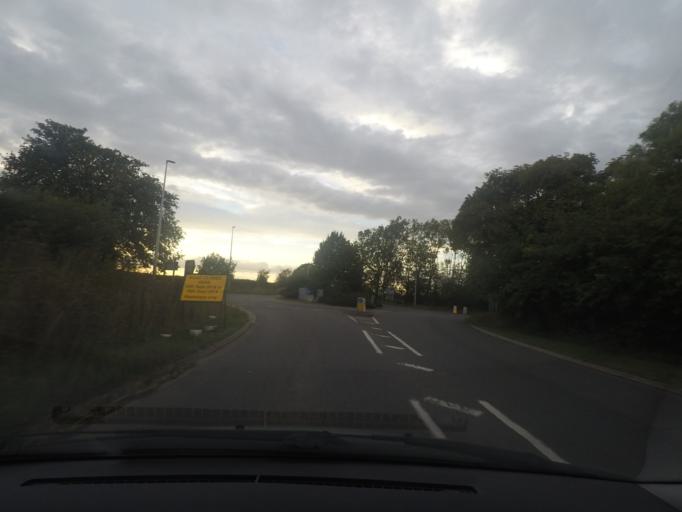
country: GB
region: England
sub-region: North East Lincolnshire
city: Wold Newton
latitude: 53.4874
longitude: -0.1293
